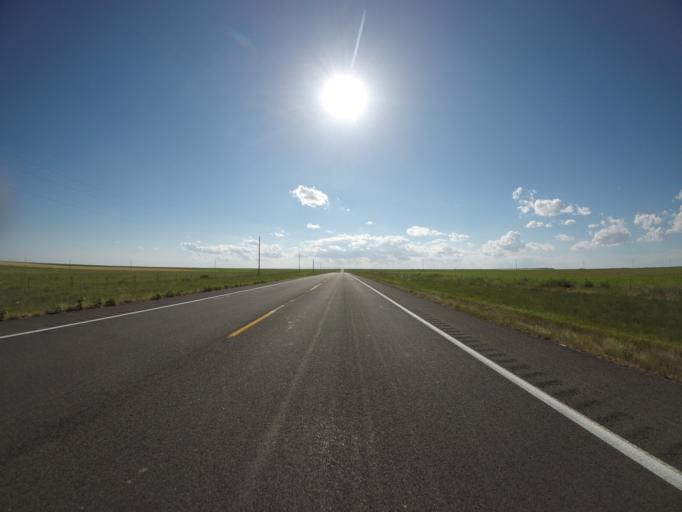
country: US
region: Colorado
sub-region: Morgan County
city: Fort Morgan
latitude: 40.6106
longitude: -103.7488
